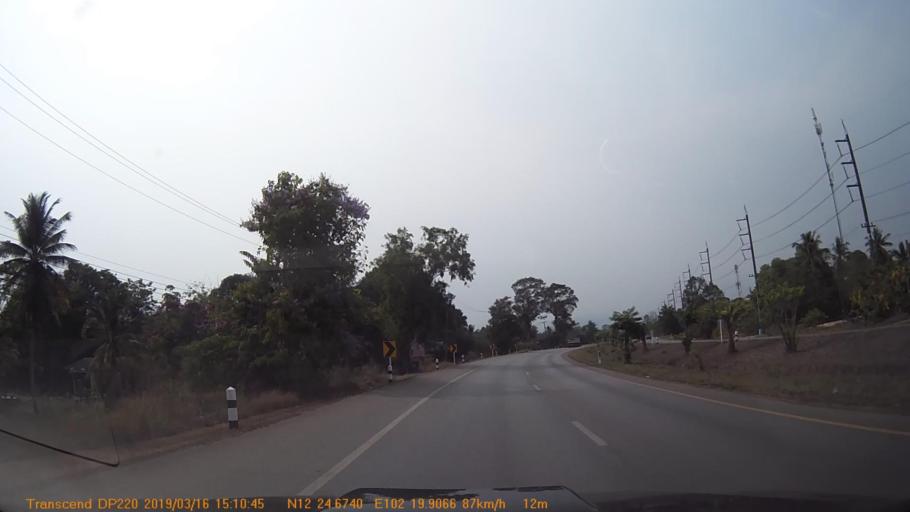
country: TH
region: Chanthaburi
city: Khlung
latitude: 12.4115
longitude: 102.3314
